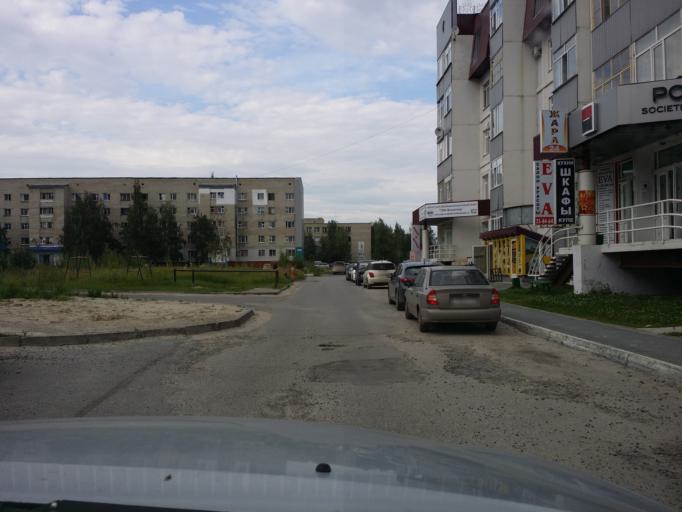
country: RU
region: Khanty-Mansiyskiy Avtonomnyy Okrug
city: Nizhnevartovsk
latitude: 60.9382
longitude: 76.5795
